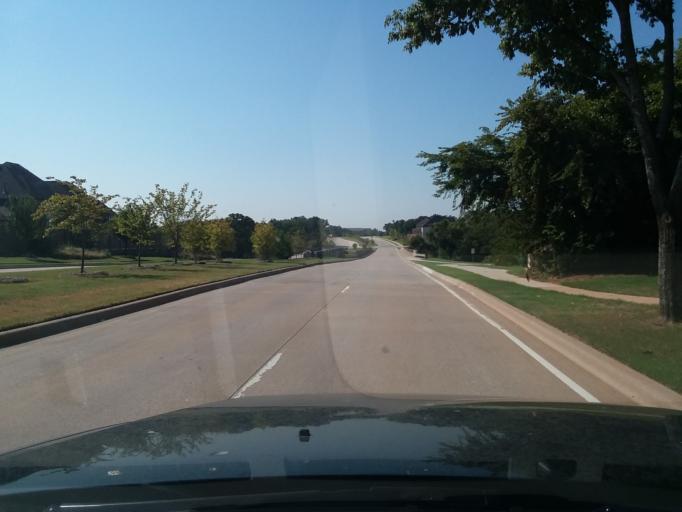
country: US
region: Texas
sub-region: Dallas County
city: Coppell
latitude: 33.0065
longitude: -97.0367
